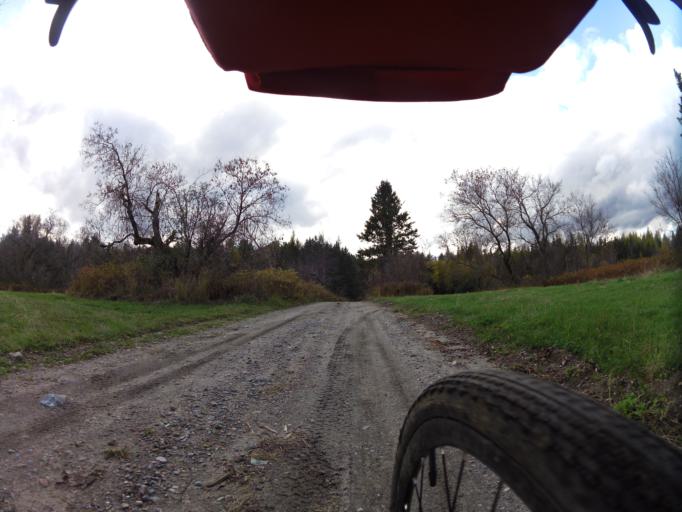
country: CA
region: Ontario
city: Arnprior
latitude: 45.6565
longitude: -76.1448
